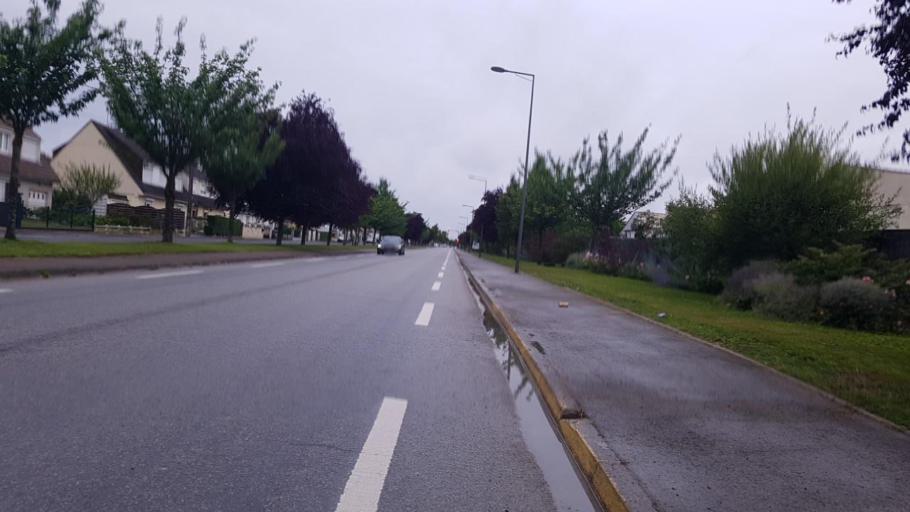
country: FR
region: Champagne-Ardenne
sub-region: Departement de la Marne
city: Saint-Memmie
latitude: 48.9347
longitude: 4.3878
